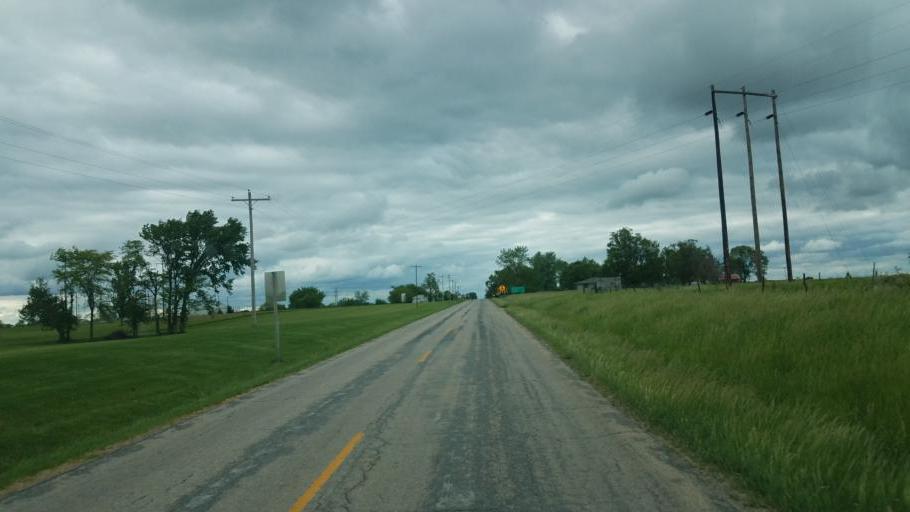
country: US
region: Missouri
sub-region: Mercer County
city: Princeton
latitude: 40.3799
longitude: -93.6800
